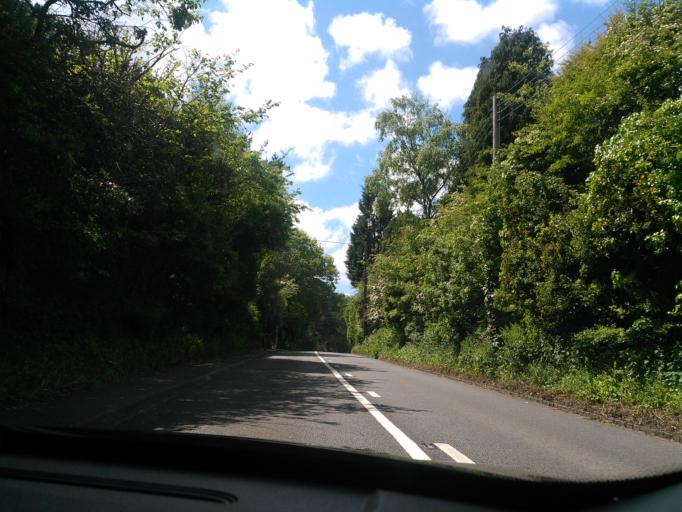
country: GB
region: England
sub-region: Staffordshire
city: Standon
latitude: 52.9245
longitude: -2.3773
